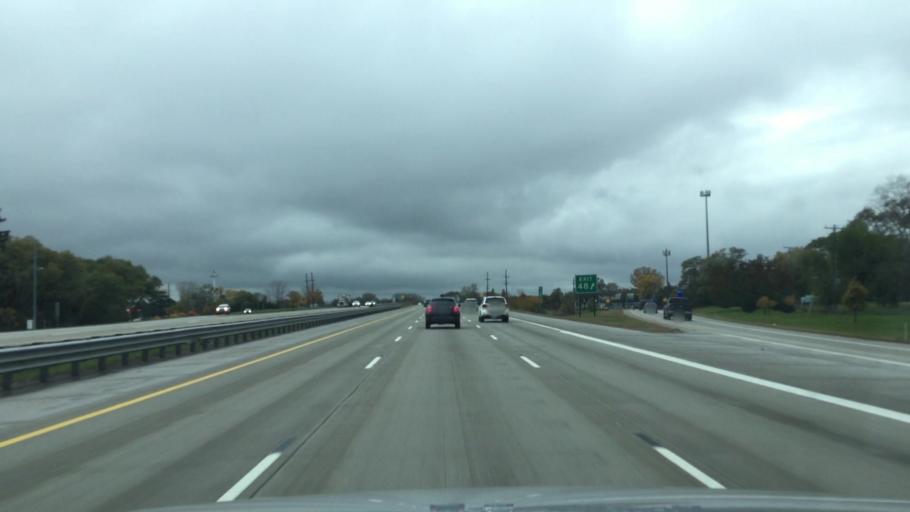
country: US
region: Michigan
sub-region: Macomb County
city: Utica
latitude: 42.6250
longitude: -83.0853
